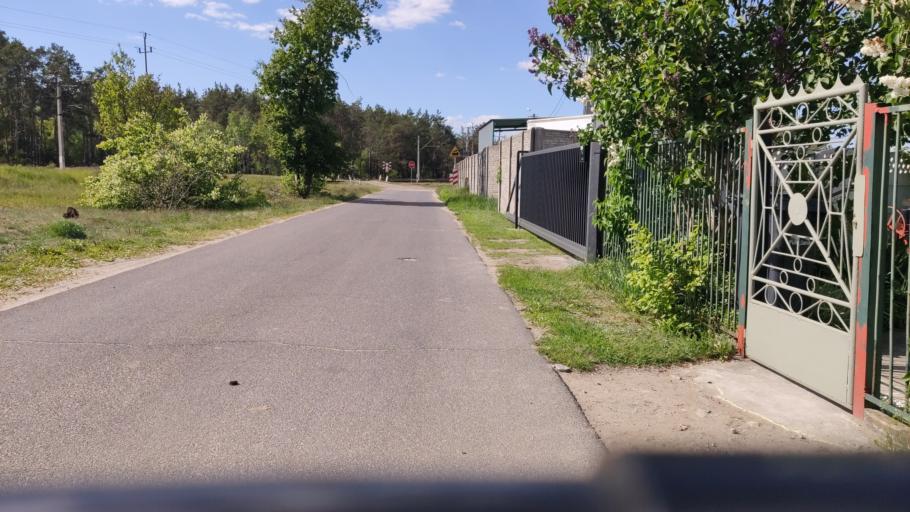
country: PL
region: Kujawsko-Pomorskie
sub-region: Wloclawek
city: Wloclawek
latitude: 52.6044
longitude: 19.0765
